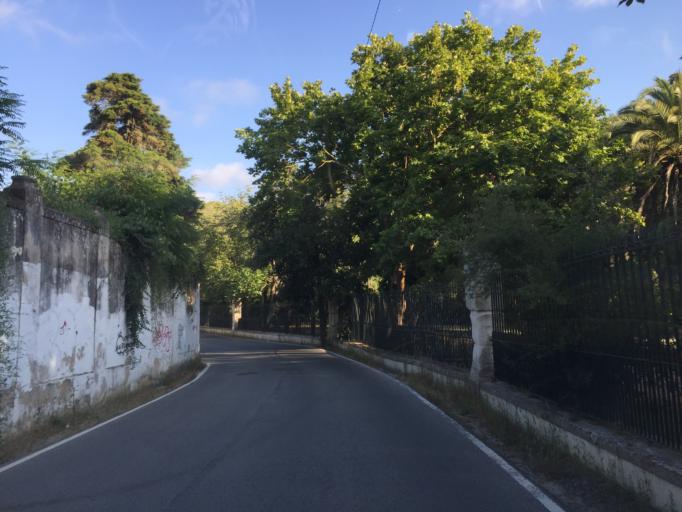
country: PT
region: Leiria
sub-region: Caldas da Rainha
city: Caldas da Rainha
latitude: 39.4011
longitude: -9.1311
